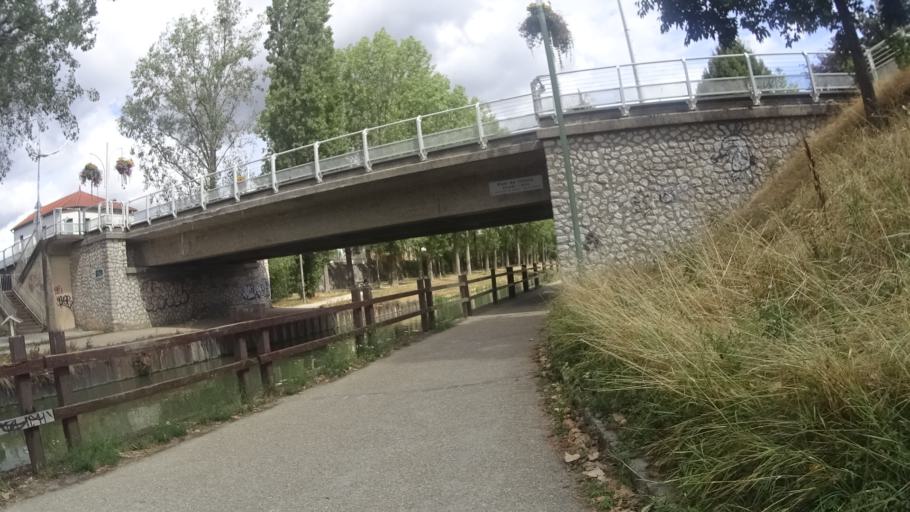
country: FR
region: Ile-de-France
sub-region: Departement de Seine-Saint-Denis
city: Les Pavillons-sous-Bois
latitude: 48.9241
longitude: 2.5128
